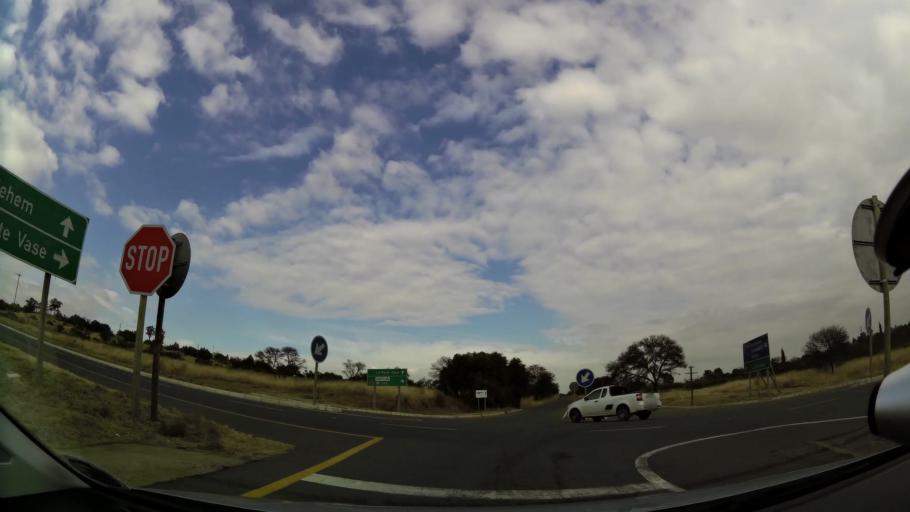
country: ZA
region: Orange Free State
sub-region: Fezile Dabi District Municipality
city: Kroonstad
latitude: -27.6879
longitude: 27.2428
